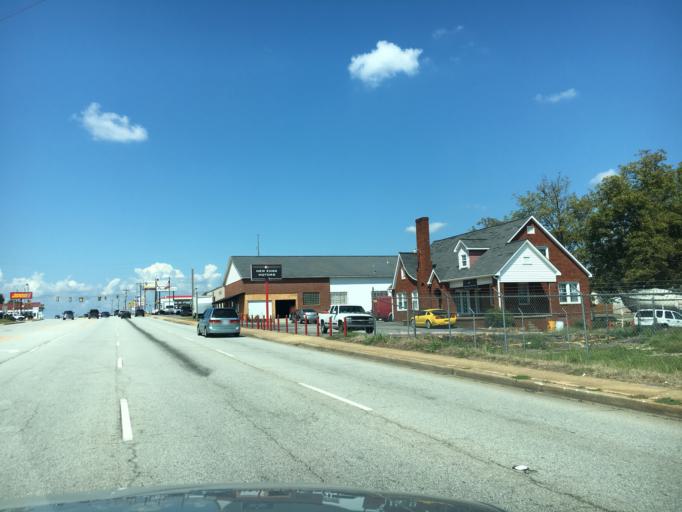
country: US
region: South Carolina
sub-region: Spartanburg County
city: Saxon
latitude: 34.9732
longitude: -81.9563
